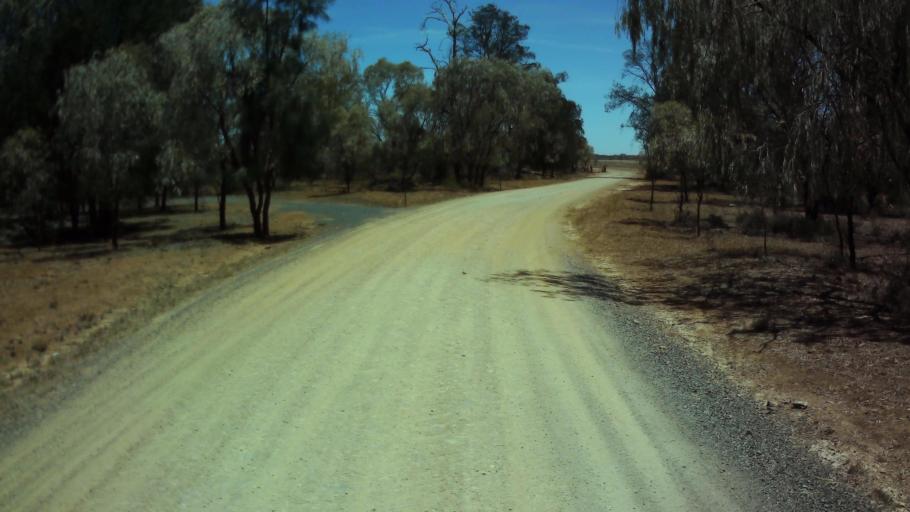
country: AU
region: New South Wales
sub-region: Bland
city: West Wyalong
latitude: -33.8175
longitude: 147.6483
